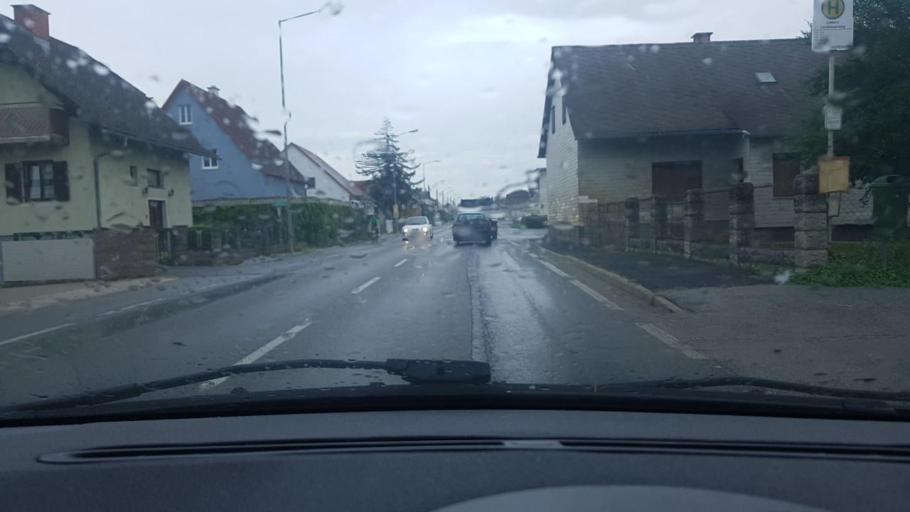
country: AT
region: Styria
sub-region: Politischer Bezirk Graz-Umgebung
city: Feldkirchen bei Graz
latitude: 47.0061
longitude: 15.4469
